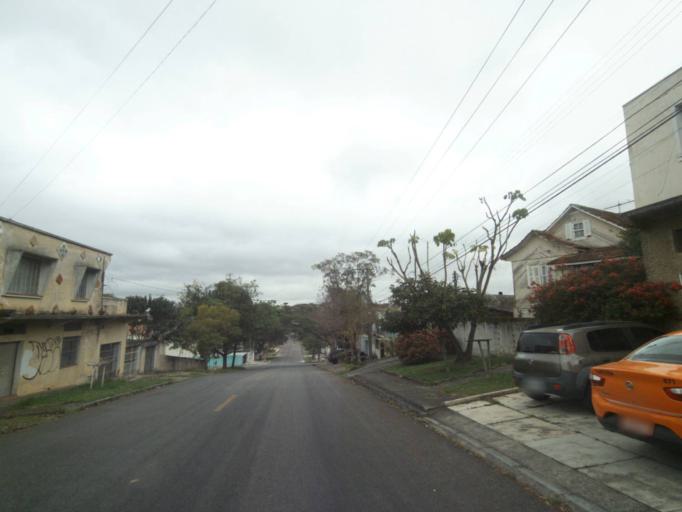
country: BR
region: Parana
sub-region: Curitiba
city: Curitiba
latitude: -25.4666
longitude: -49.2746
